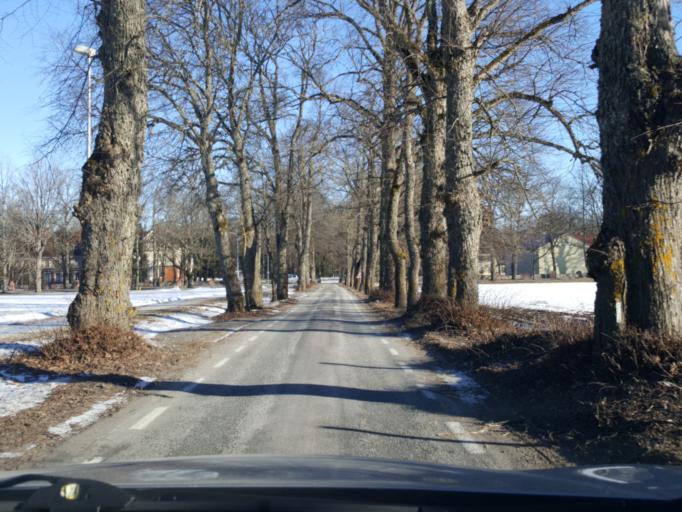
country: EE
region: Viljandimaa
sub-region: Vohma linn
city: Vohma
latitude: 58.5526
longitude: 25.5603
